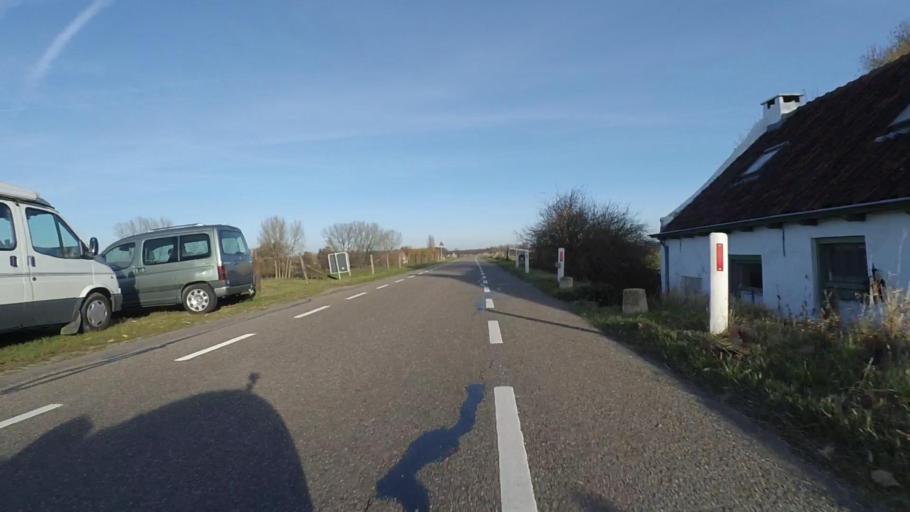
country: NL
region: Utrecht
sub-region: Gemeente Utrechtse Heuvelrug
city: Leersum
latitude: 51.9840
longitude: 5.4223
